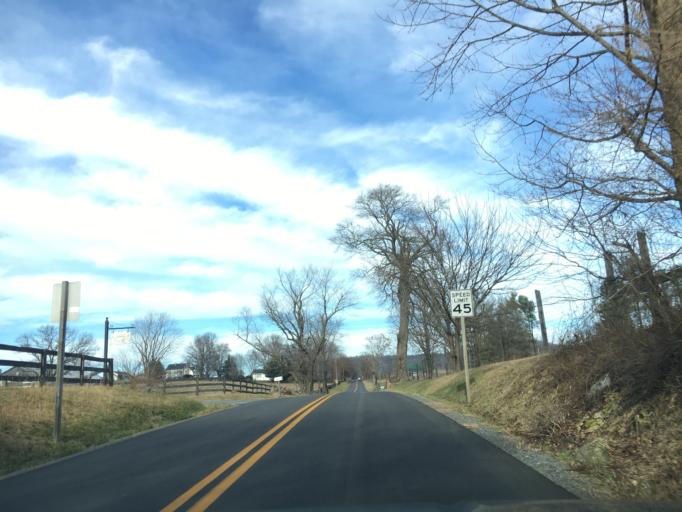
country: US
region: Virginia
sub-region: Warren County
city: Apple Mountain Lake
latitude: 38.8524
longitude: -77.9960
